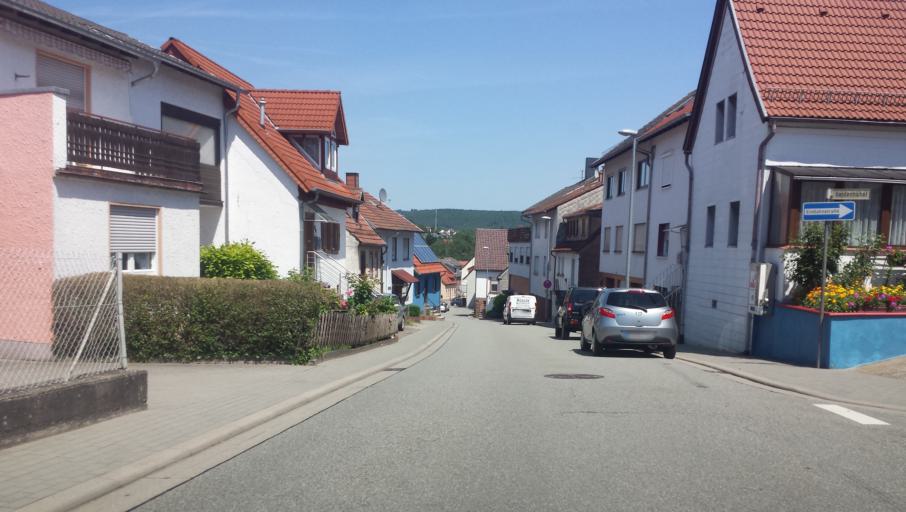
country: DE
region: Rheinland-Pfalz
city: Hochspeyer
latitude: 49.4399
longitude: 7.8938
